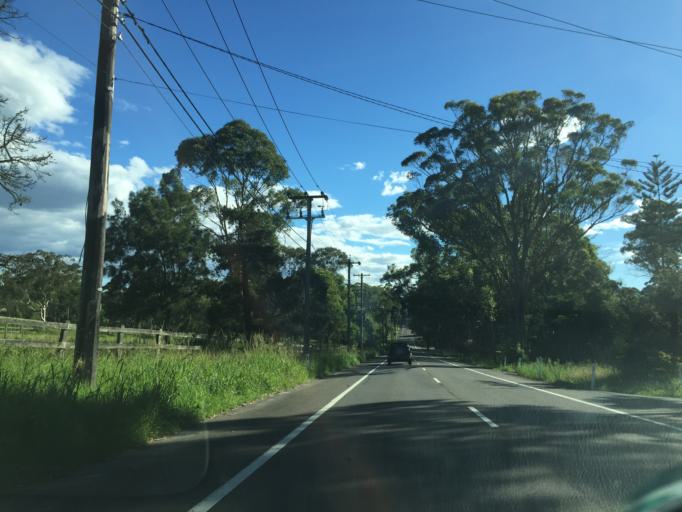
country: AU
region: New South Wales
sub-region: Hornsby Shire
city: Galston
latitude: -33.6717
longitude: 151.0358
